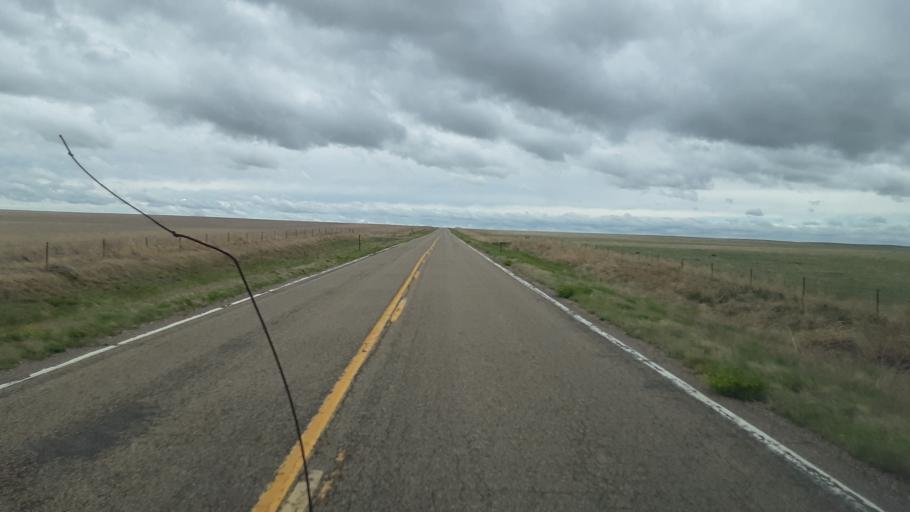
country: US
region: Colorado
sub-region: Lincoln County
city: Hugo
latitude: 38.8512
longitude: -103.6280
